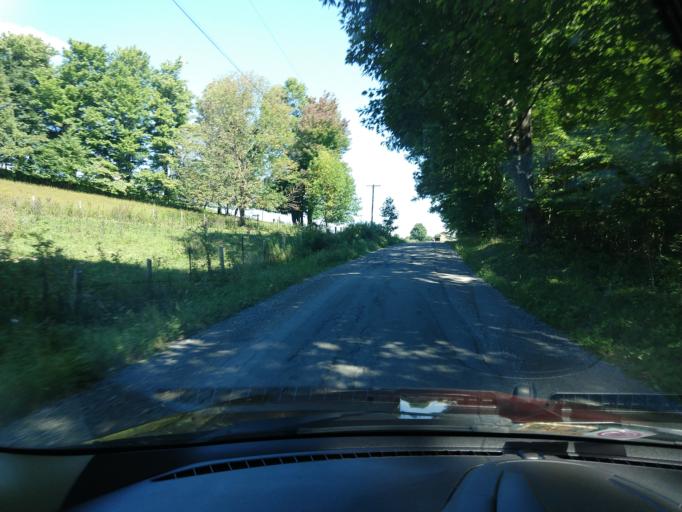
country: US
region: West Virginia
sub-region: Nicholas County
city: Craigsville
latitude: 38.2416
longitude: -80.7088
